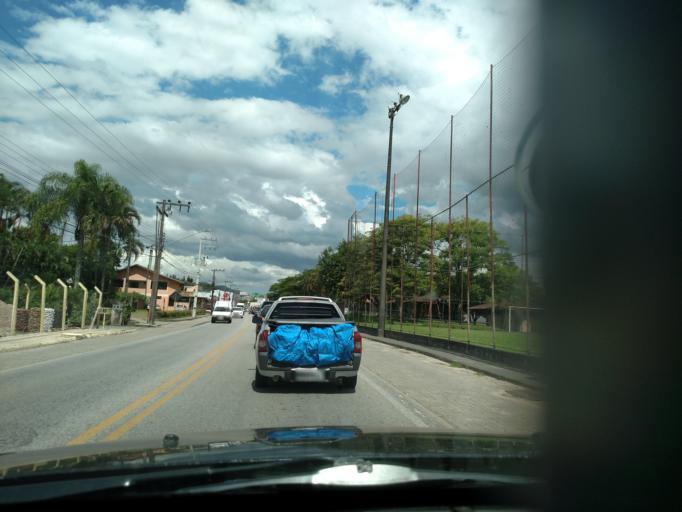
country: BR
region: Santa Catarina
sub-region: Gaspar
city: Gaspar
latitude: -26.9259
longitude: -48.9666
